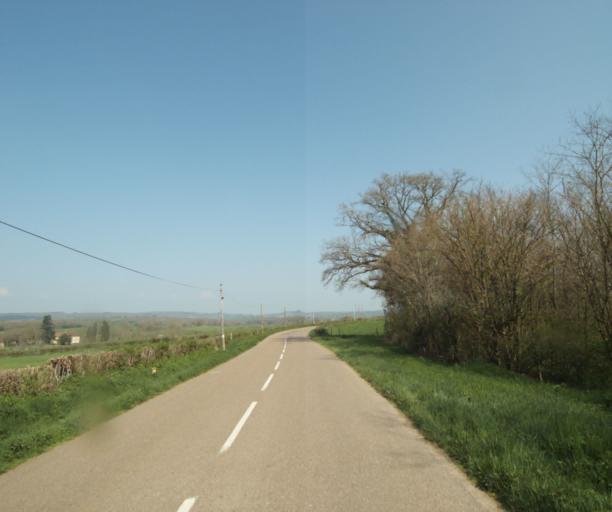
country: FR
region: Bourgogne
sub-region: Departement de Saone-et-Loire
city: Charolles
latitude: 46.4852
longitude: 4.3444
